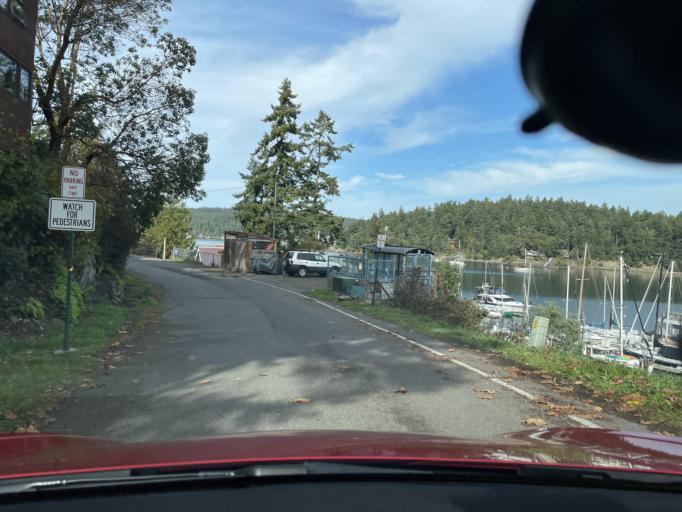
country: US
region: Washington
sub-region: San Juan County
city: Friday Harbor
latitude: 48.5329
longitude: -123.0062
